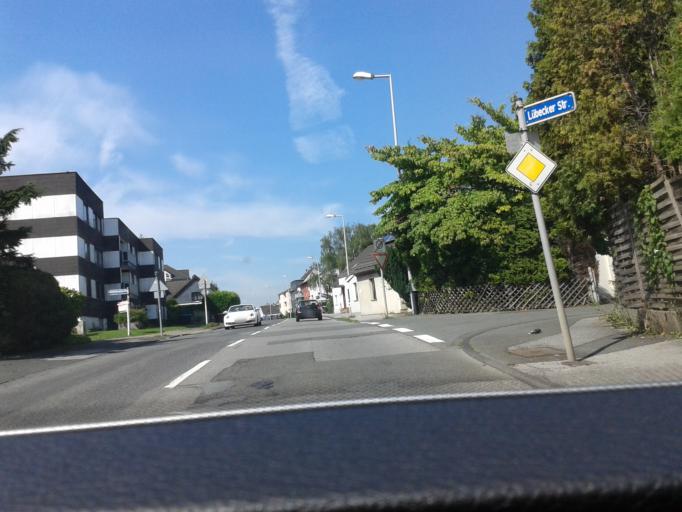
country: DE
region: North Rhine-Westphalia
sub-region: Regierungsbezirk Dusseldorf
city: Muelheim (Ruhr)
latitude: 51.4108
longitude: 6.8620
